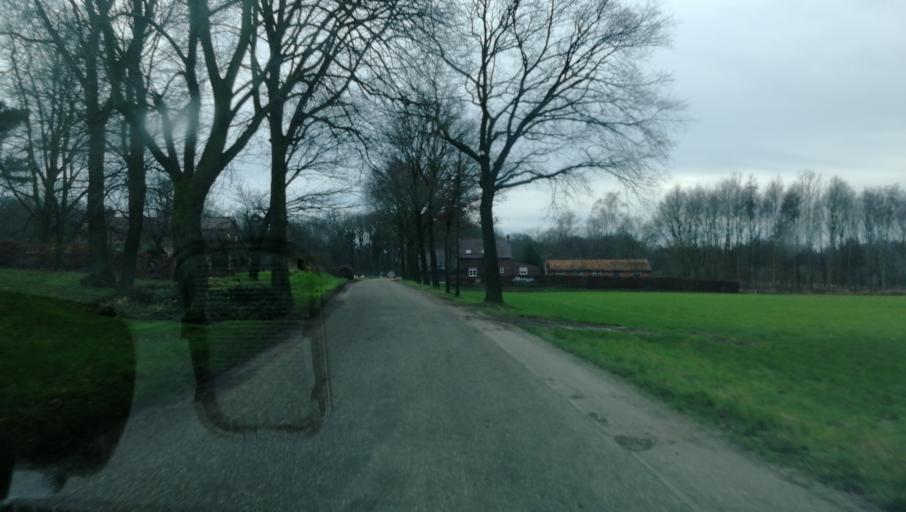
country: NL
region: Limburg
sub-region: Gemeente Venlo
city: Venlo
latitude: 51.4126
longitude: 6.1923
